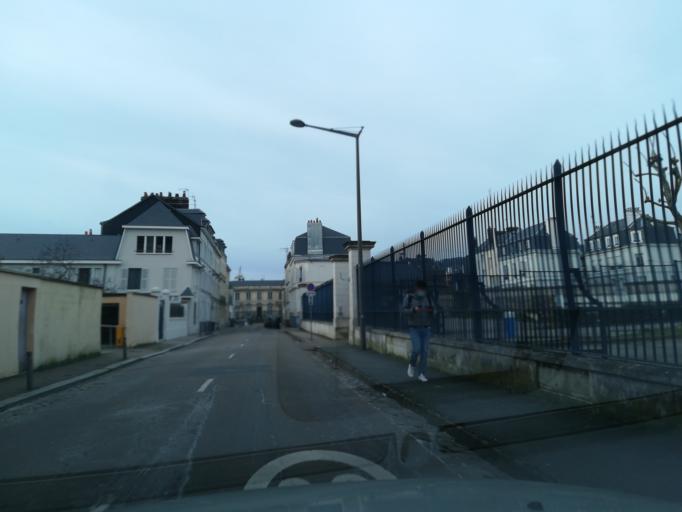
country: FR
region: Haute-Normandie
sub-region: Departement de la Seine-Maritime
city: Rouen
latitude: 49.4457
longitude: 1.0793
